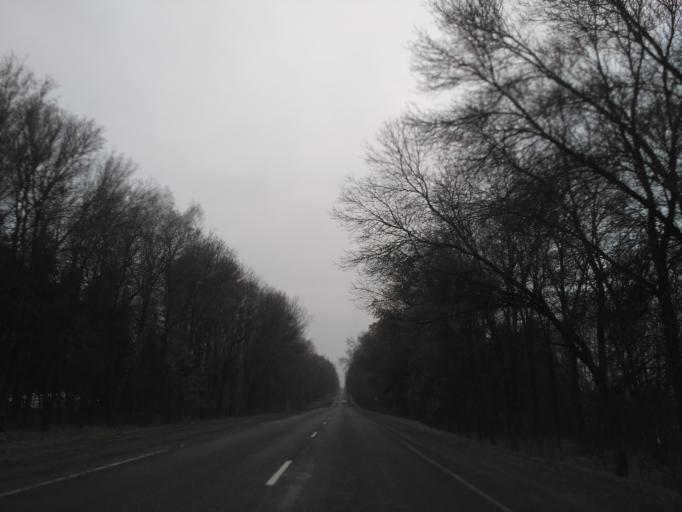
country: BY
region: Minsk
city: Snow
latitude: 53.2391
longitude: 26.2395
